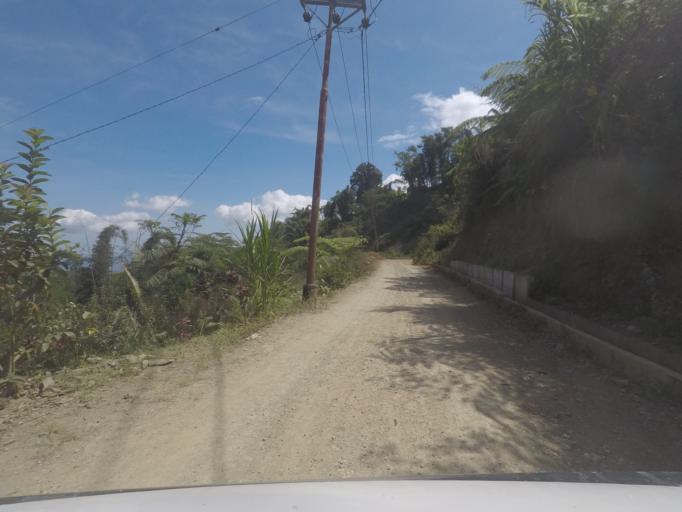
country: TL
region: Ermera
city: Gleno
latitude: -8.7529
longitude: 125.3297
